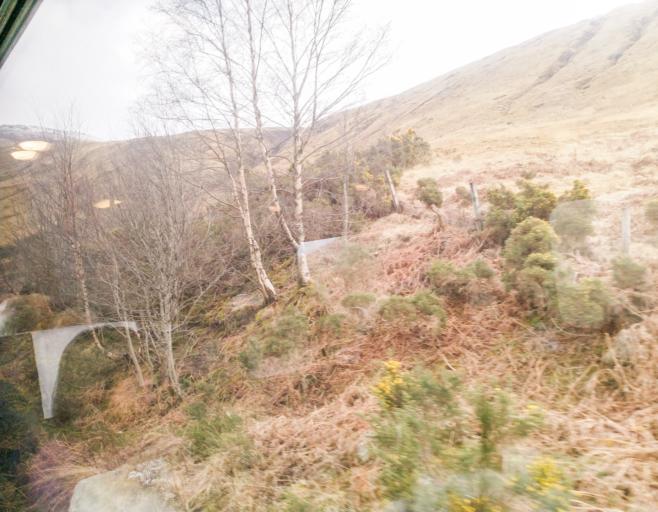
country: GB
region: Scotland
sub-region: Highland
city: Spean Bridge
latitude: 56.8115
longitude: -4.7170
